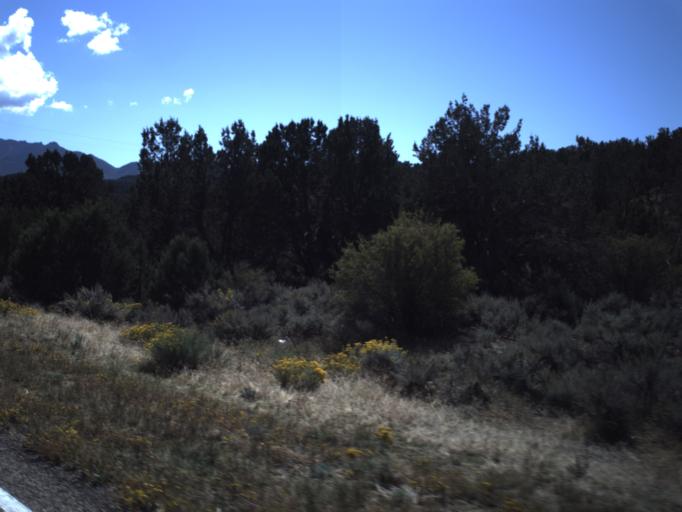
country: US
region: Utah
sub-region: Washington County
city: Enterprise
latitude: 37.4583
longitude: -113.6287
